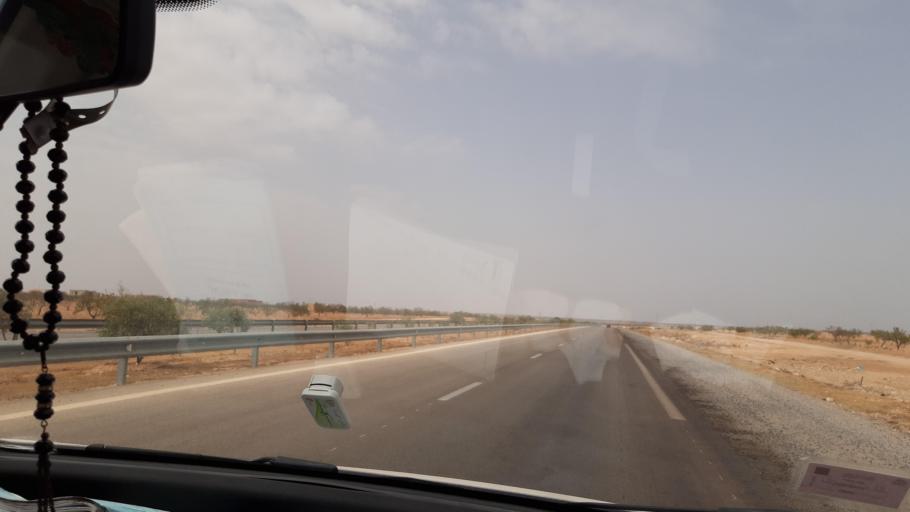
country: TN
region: Safaqis
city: Sfax
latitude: 34.8606
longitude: 10.6861
